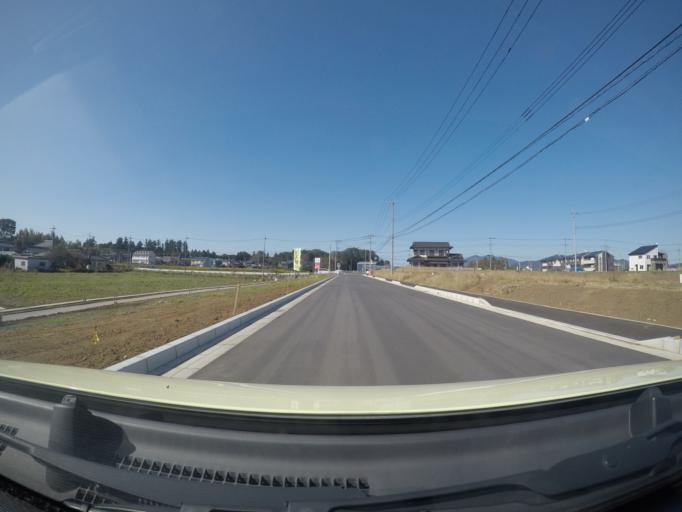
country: JP
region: Ibaraki
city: Naka
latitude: 36.1037
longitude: 140.1214
